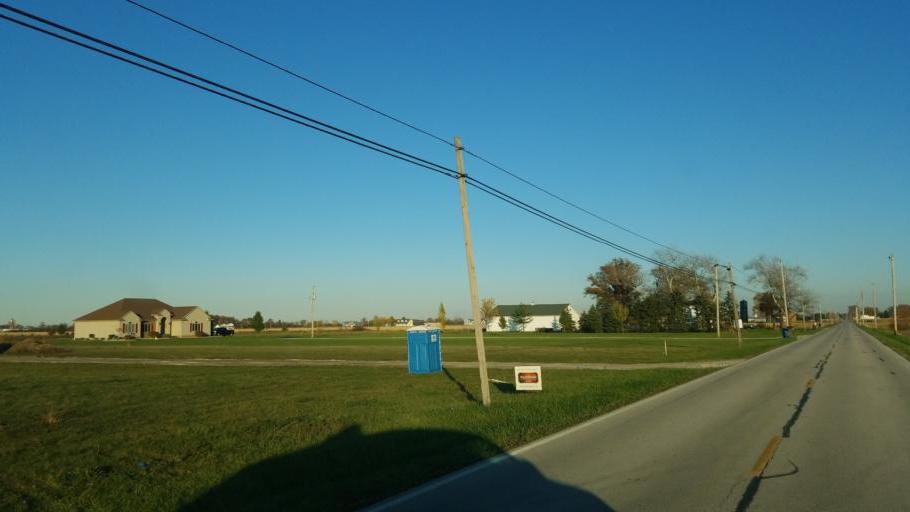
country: US
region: Ohio
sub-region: Sandusky County
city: Green Springs
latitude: 41.3068
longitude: -83.0302
